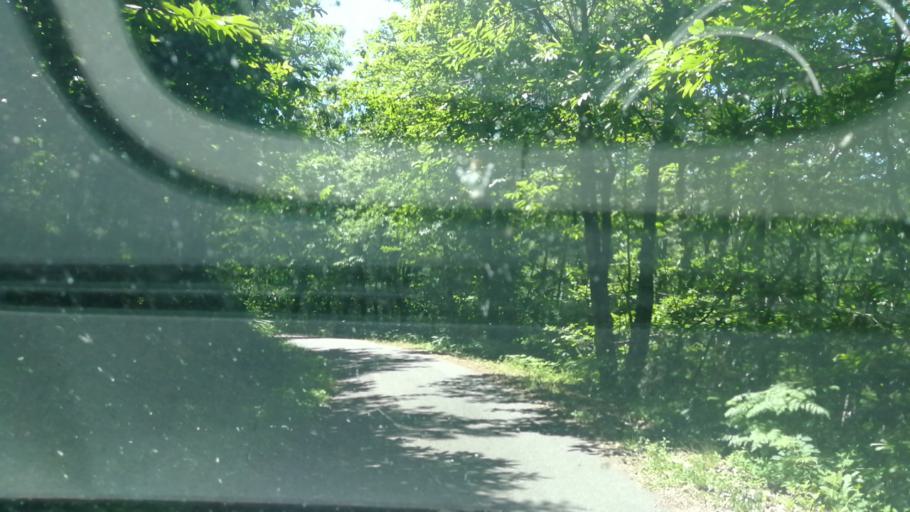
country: FR
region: Midi-Pyrenees
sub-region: Departement de l'Aveyron
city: Firmi
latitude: 44.5850
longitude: 2.3821
